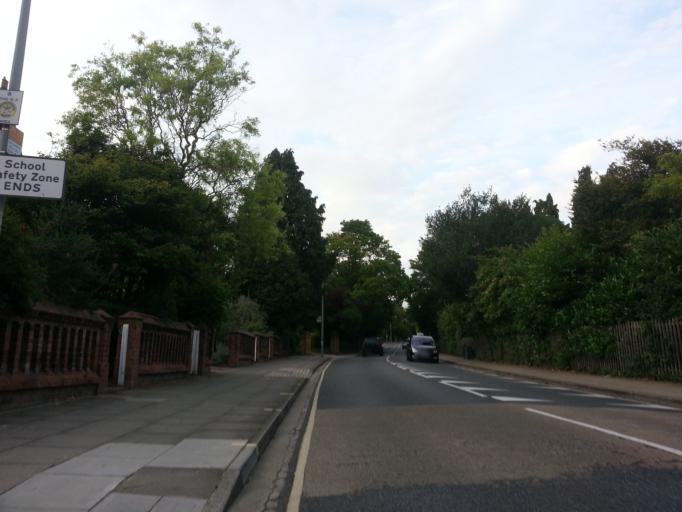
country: GB
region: England
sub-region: Suffolk
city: Ipswich
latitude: 52.0652
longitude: 1.1521
